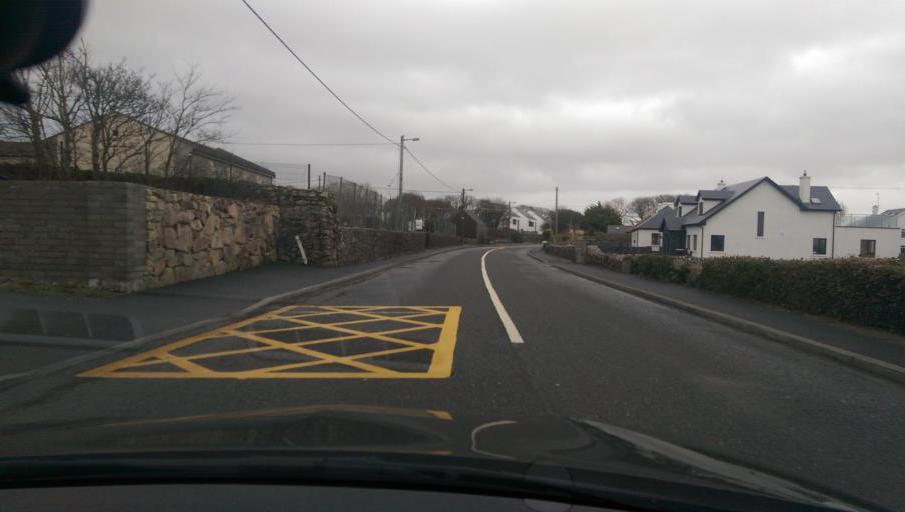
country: IE
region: Connaught
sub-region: County Galway
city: Bearna
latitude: 53.2519
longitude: -9.1477
